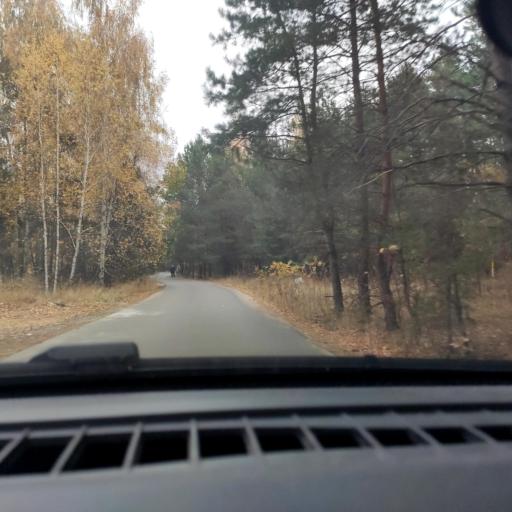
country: RU
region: Voronezj
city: Podgornoye
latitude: 51.7643
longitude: 39.1881
